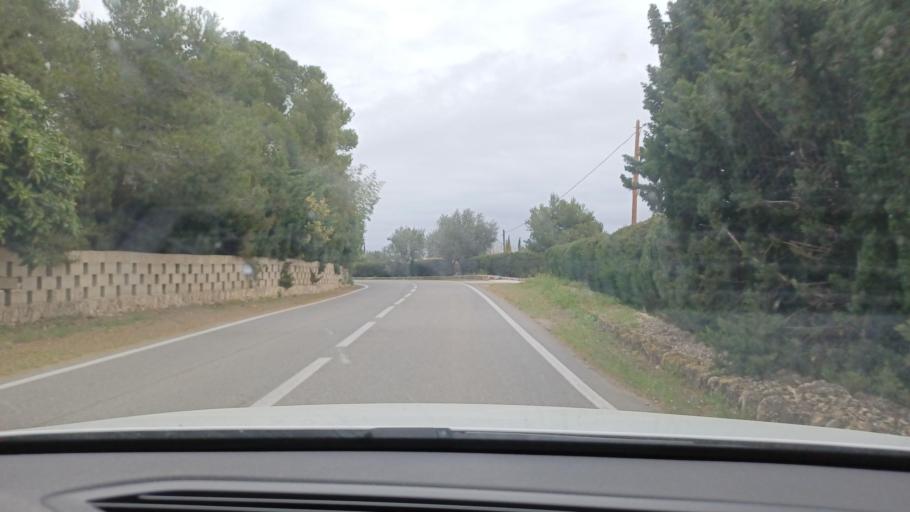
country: ES
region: Catalonia
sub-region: Provincia de Tarragona
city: Tortosa
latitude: 40.7945
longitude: 0.4623
